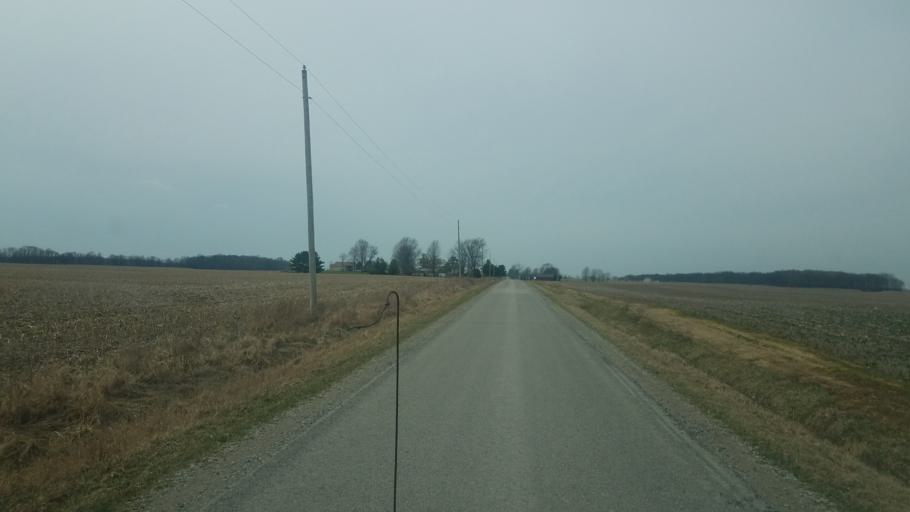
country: US
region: Ohio
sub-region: Huron County
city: Greenwich
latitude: 41.1445
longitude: -82.5035
